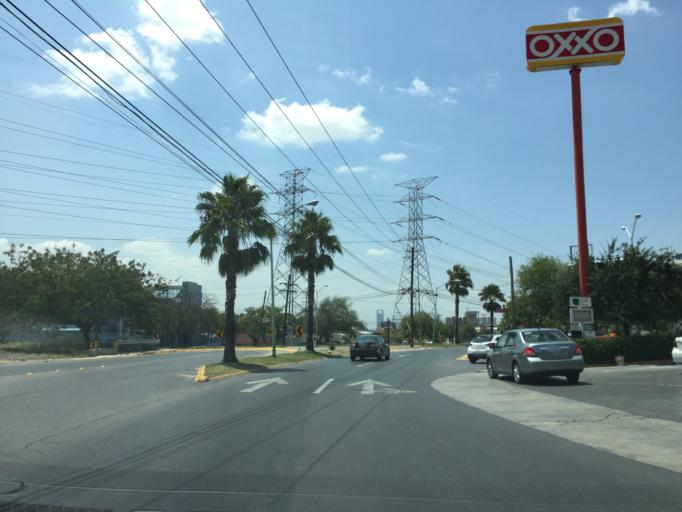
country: MX
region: Nuevo Leon
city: Guadalupe
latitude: 25.6416
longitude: -100.2682
